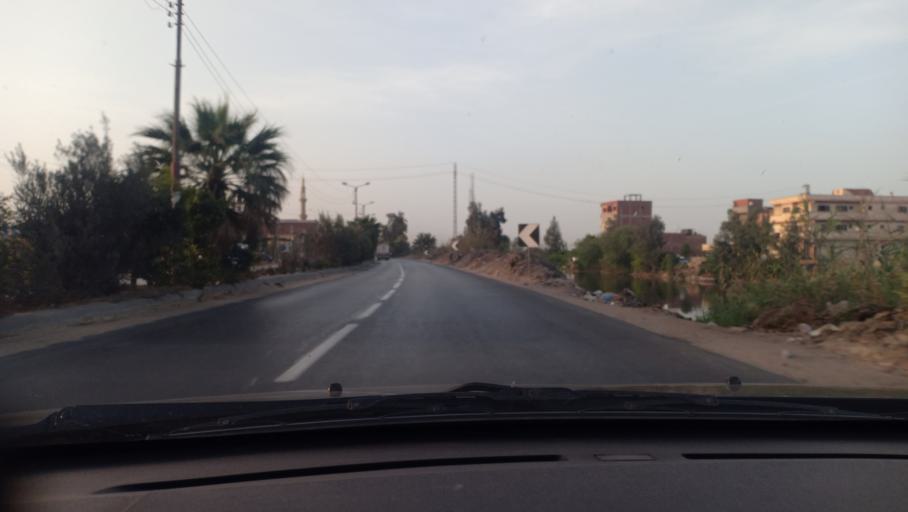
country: EG
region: Muhafazat al Gharbiyah
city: Zifta
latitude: 30.6433
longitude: 31.2822
